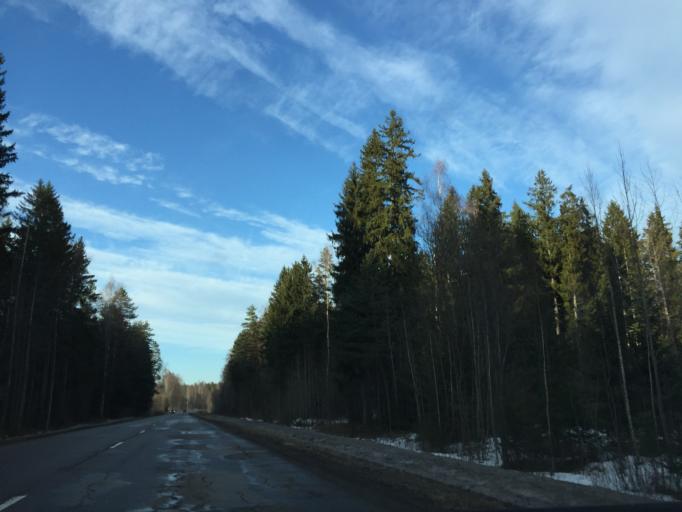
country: LV
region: Kekava
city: Balozi
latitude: 56.7467
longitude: 24.1077
